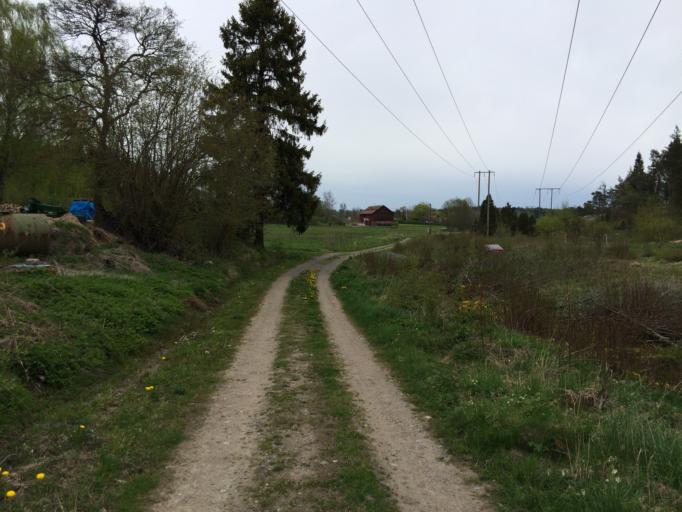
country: SE
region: Stockholm
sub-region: Norrtalje Kommun
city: Norrtalje
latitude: 59.6566
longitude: 18.6628
